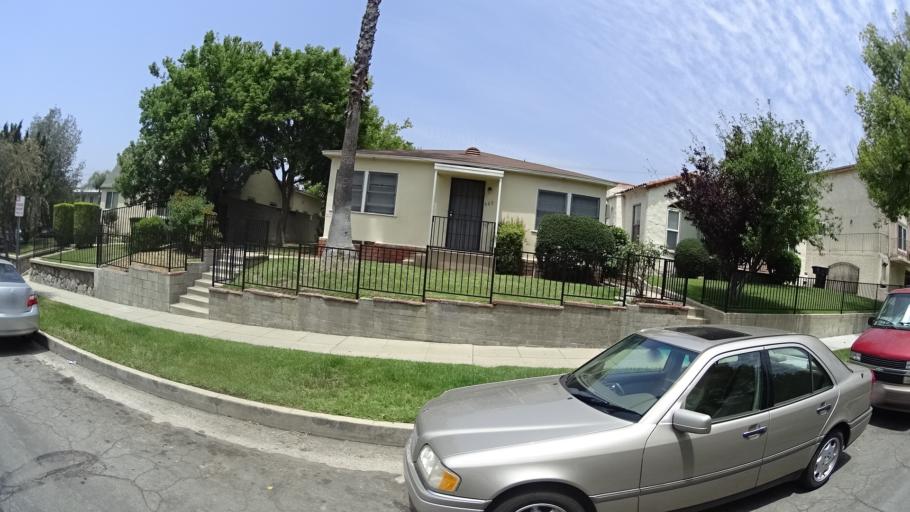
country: US
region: California
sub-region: Los Angeles County
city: Burbank
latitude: 34.1883
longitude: -118.3096
